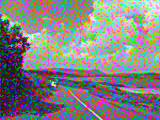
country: IE
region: Ulster
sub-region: County Donegal
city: Ramelton
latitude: 55.1847
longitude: -7.6014
